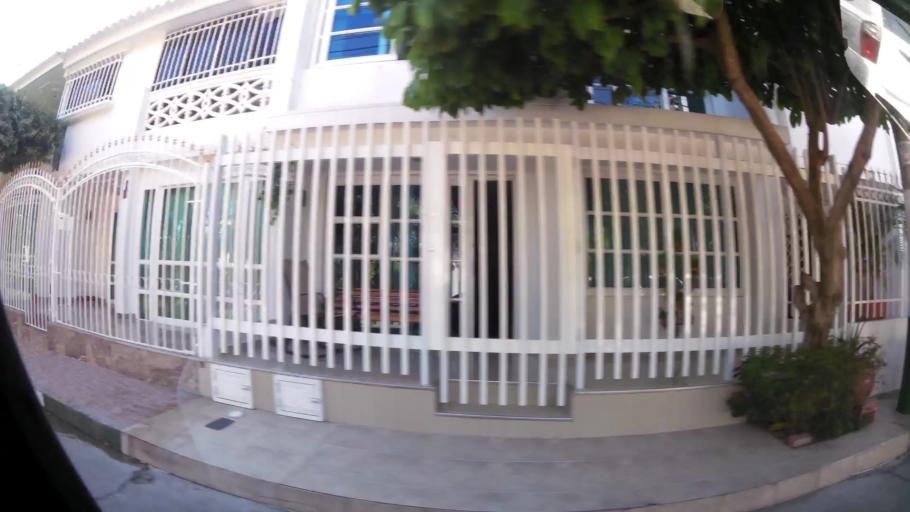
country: CO
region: Bolivar
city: Cartagena
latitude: 10.3889
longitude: -75.4739
